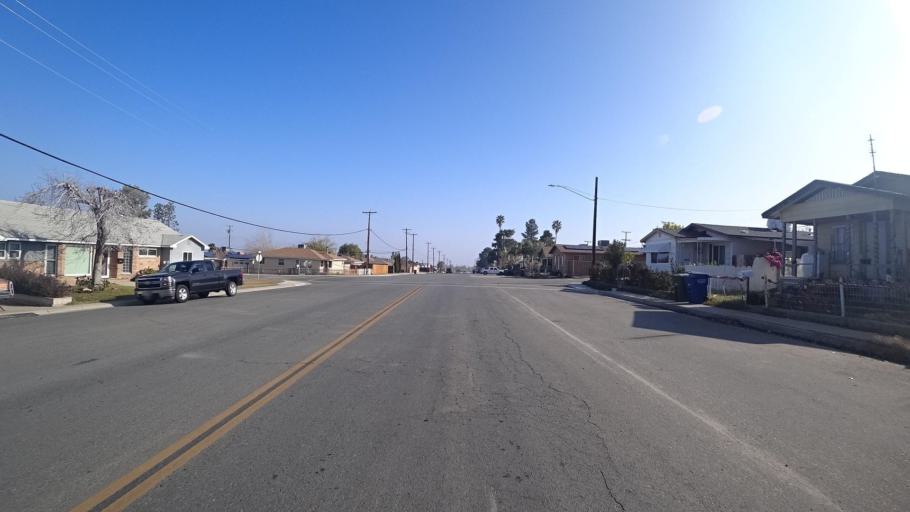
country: US
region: California
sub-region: Kern County
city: Taft Heights
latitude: 35.1368
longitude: -119.4697
